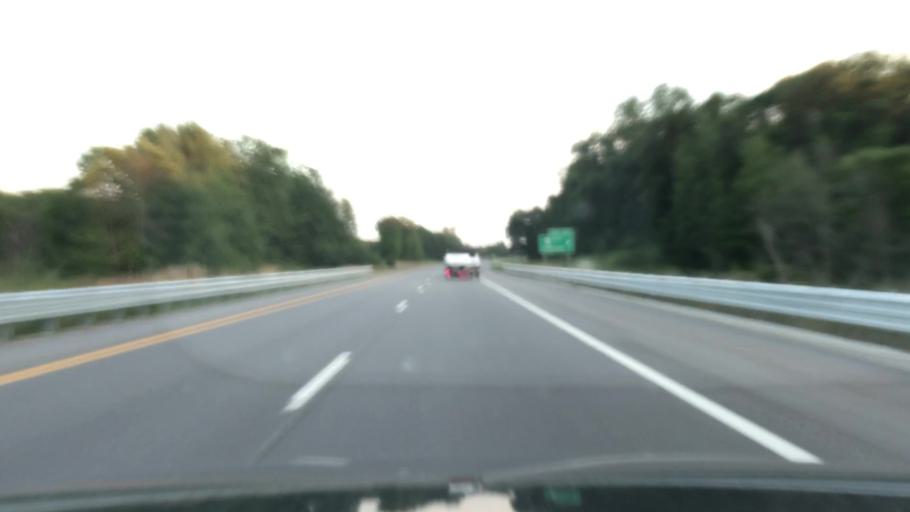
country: US
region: Michigan
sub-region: Montcalm County
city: Howard City
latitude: 43.4336
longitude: -85.4940
